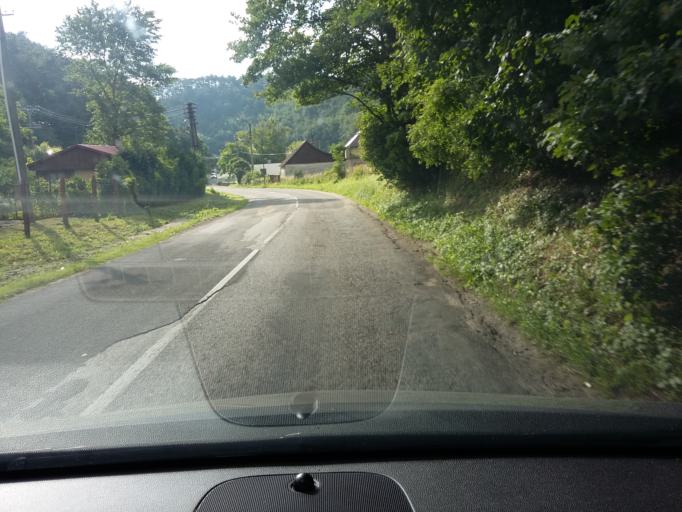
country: SK
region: Trnavsky
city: Smolenice
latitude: 48.5431
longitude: 17.4036
